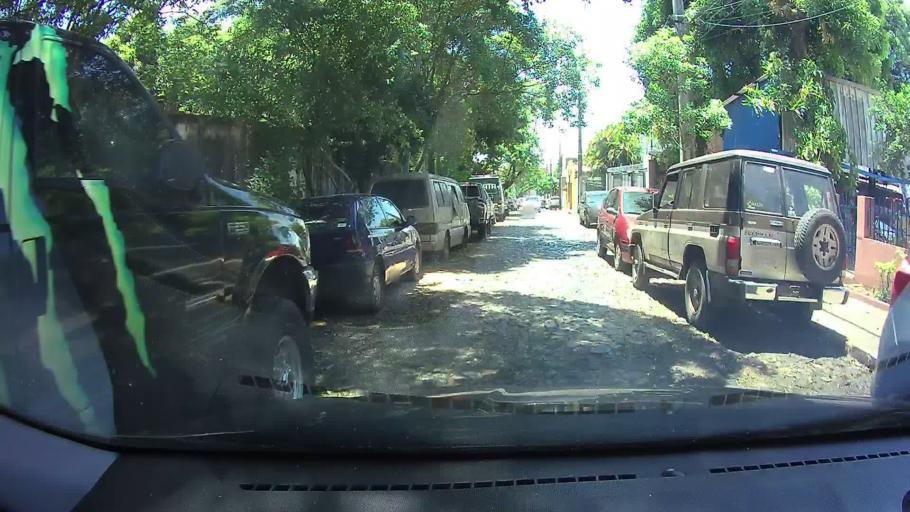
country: PY
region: Central
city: Lambare
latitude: -25.3110
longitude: -57.5947
